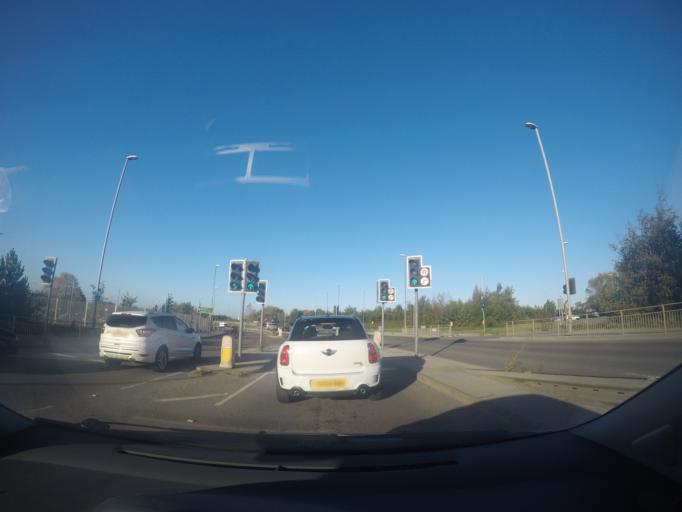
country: GB
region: England
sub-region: City and Borough of Leeds
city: Leeds
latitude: 53.7886
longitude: -1.5102
